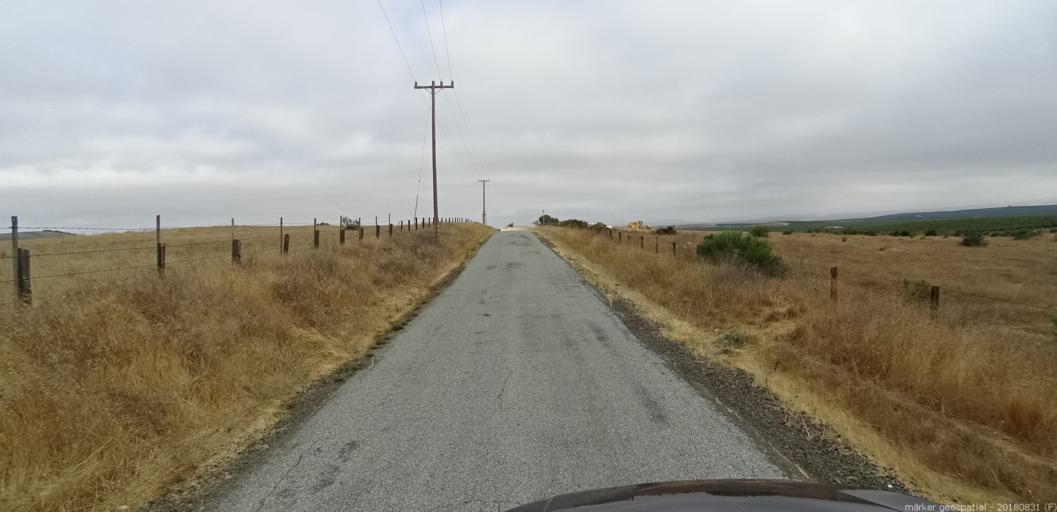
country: US
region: California
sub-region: Monterey County
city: King City
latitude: 36.1308
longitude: -121.0901
